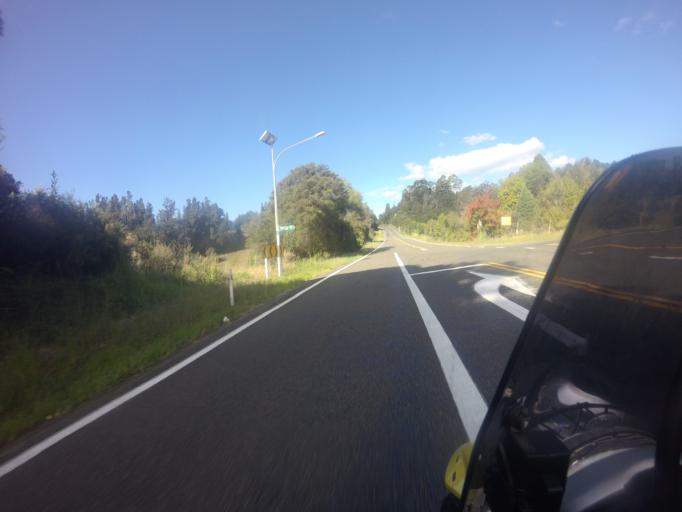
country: NZ
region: Bay of Plenty
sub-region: Whakatane District
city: Whakatane
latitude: -38.0180
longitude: 177.0711
